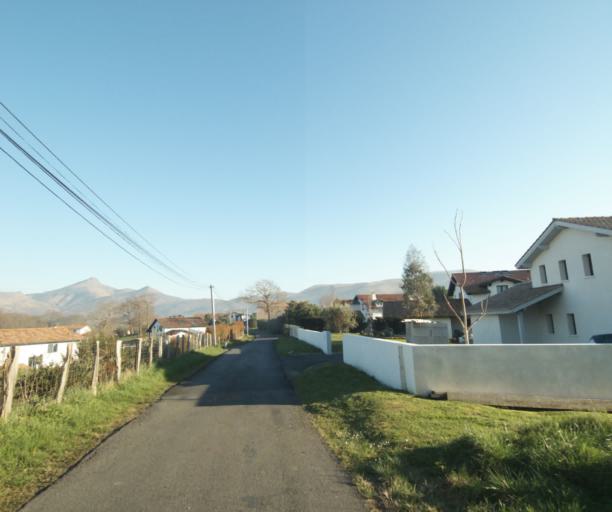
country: FR
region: Aquitaine
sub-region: Departement des Pyrenees-Atlantiques
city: Urrugne
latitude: 43.3459
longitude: -1.7024
